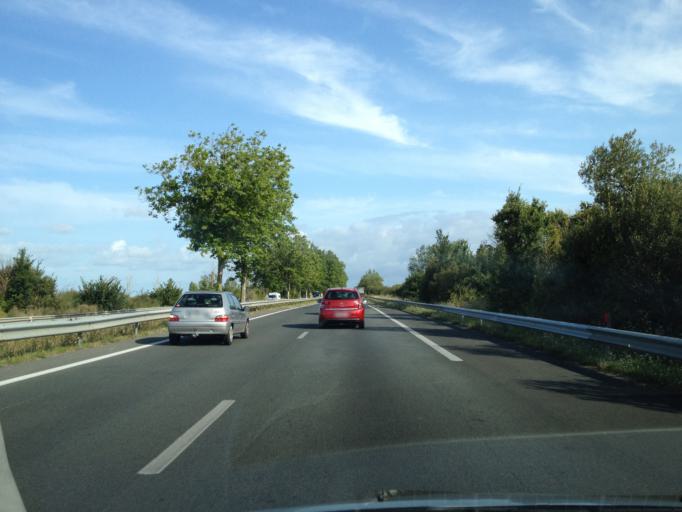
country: FR
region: Poitou-Charentes
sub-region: Departement de la Charente-Maritime
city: Yves
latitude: 46.0510
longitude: -1.0520
